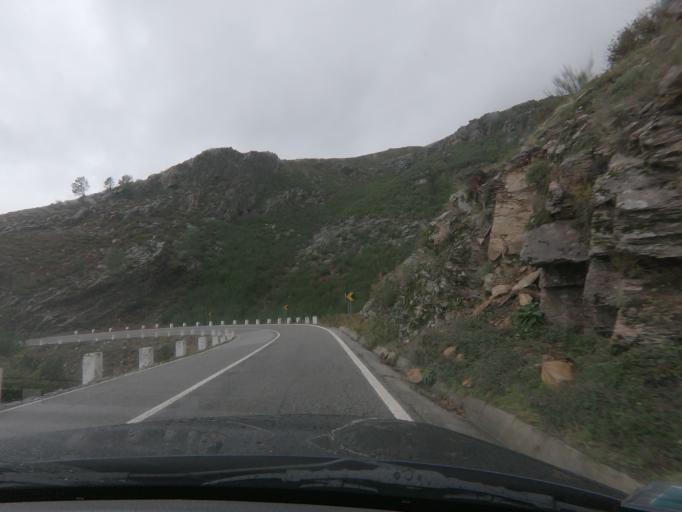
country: PT
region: Vila Real
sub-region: Mondim de Basto
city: Mondim de Basto
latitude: 41.3441
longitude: -7.8715
